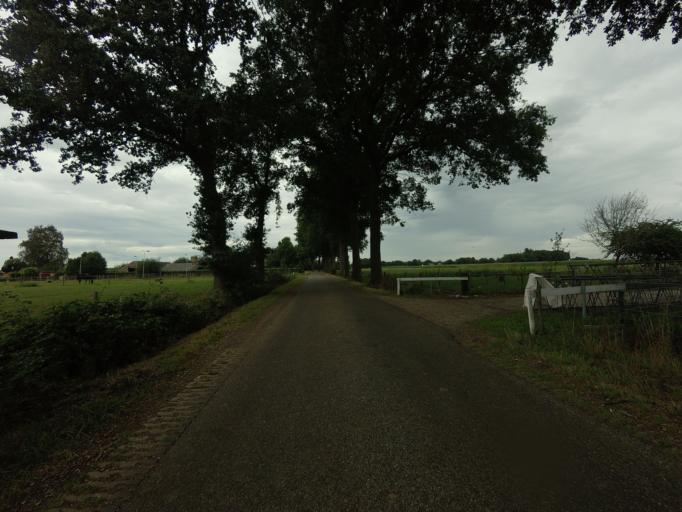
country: NL
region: Overijssel
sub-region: Gemeente Raalte
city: Raalte
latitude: 52.3589
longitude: 6.3565
